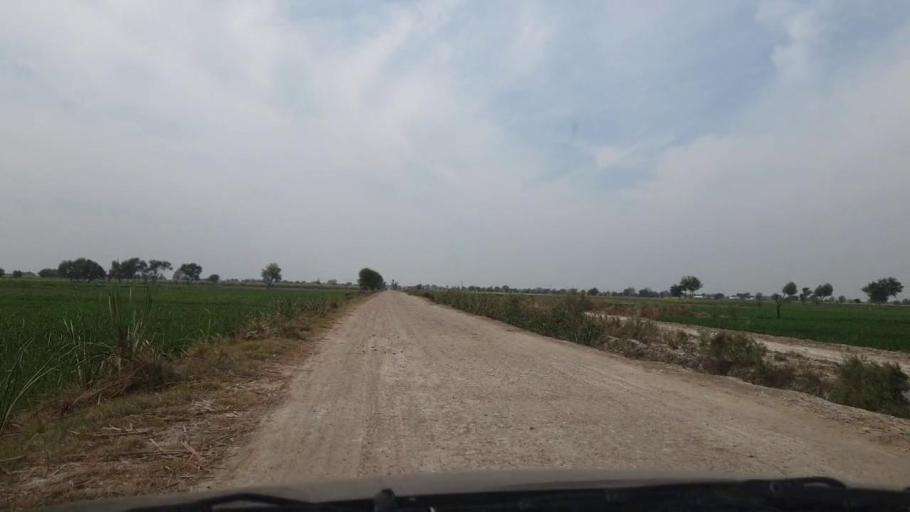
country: PK
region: Sindh
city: Sinjhoro
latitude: 26.0830
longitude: 68.8346
